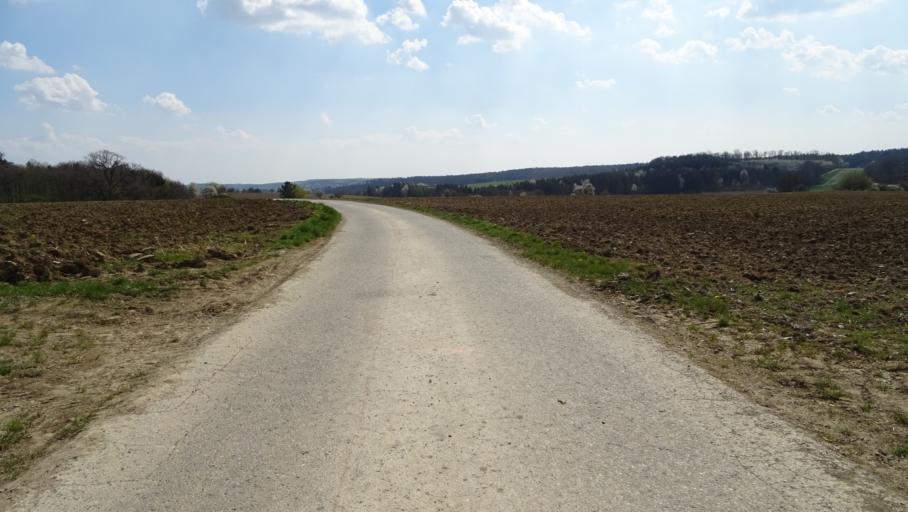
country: DE
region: Baden-Wuerttemberg
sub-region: Karlsruhe Region
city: Billigheim
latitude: 49.3865
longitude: 9.2557
